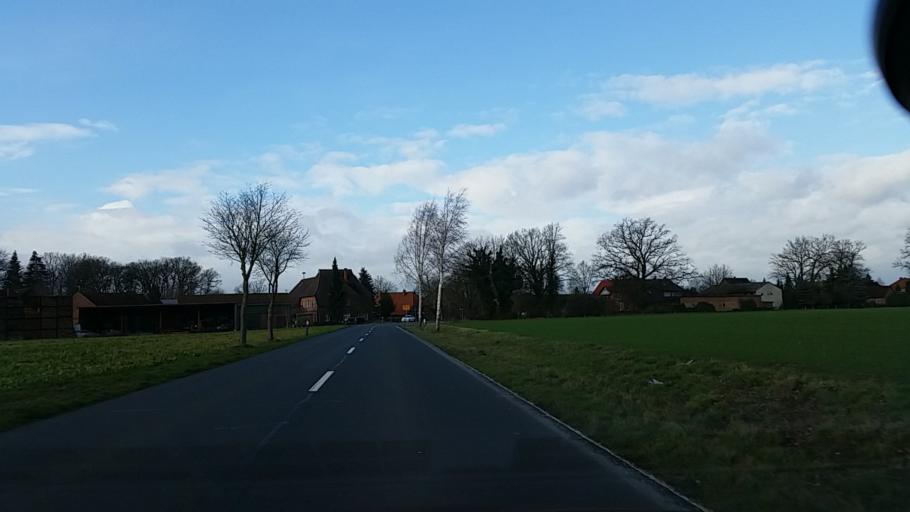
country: DE
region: Lower Saxony
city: Wrestedt
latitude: 52.9118
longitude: 10.5406
